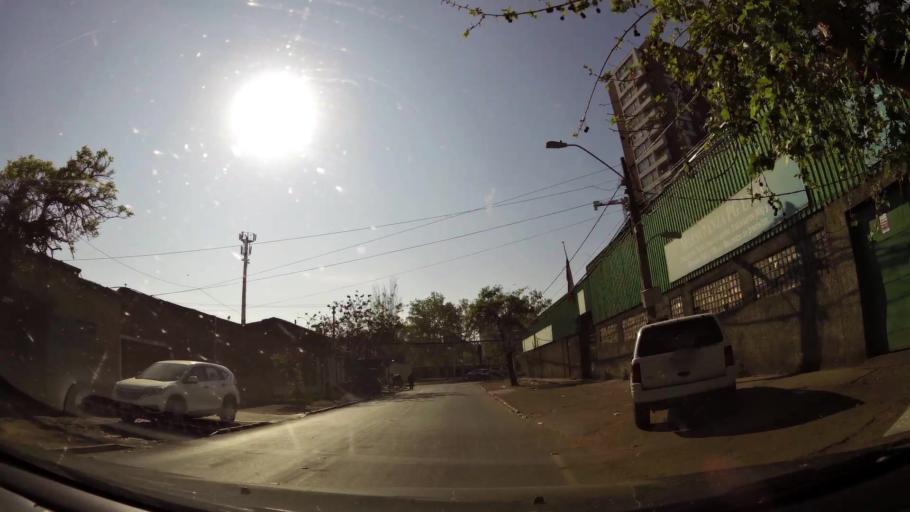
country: CL
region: Santiago Metropolitan
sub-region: Provincia de Santiago
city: Santiago
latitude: -33.4062
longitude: -70.6688
